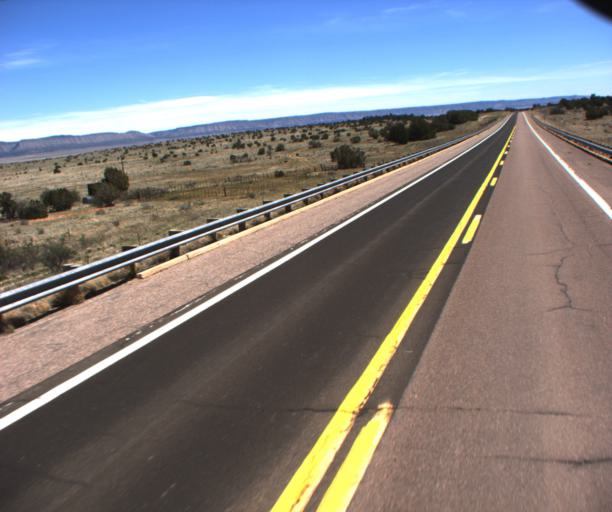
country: US
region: Arizona
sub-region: Mohave County
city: Peach Springs
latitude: 35.5187
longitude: -113.2024
